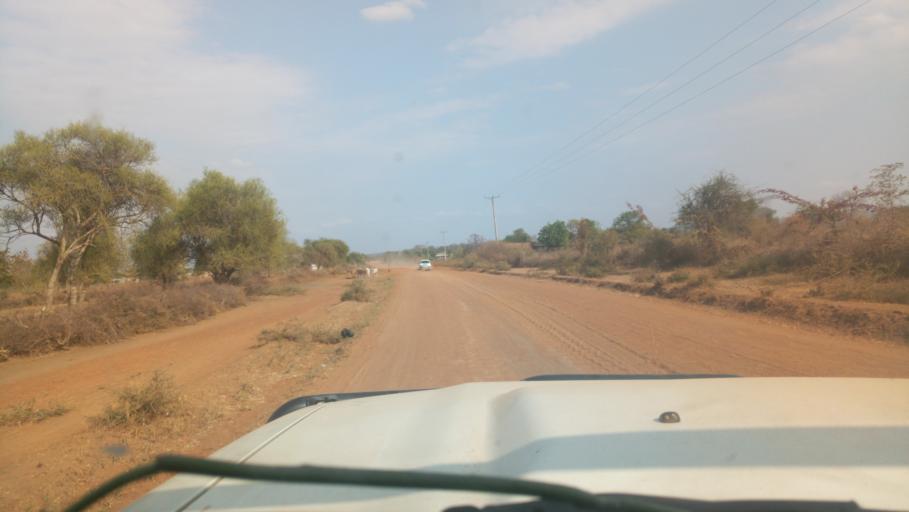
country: KE
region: Kitui
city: Kitui
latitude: -1.6589
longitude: 37.9144
